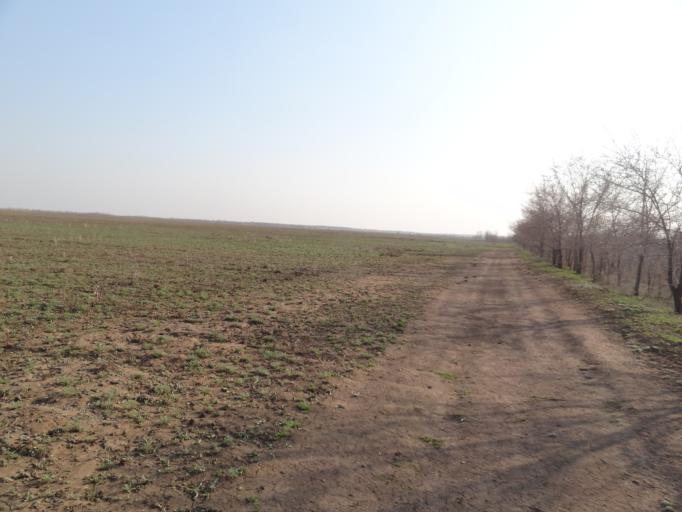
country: RU
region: Saratov
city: Privolzhskiy
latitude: 51.3249
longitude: 46.0317
